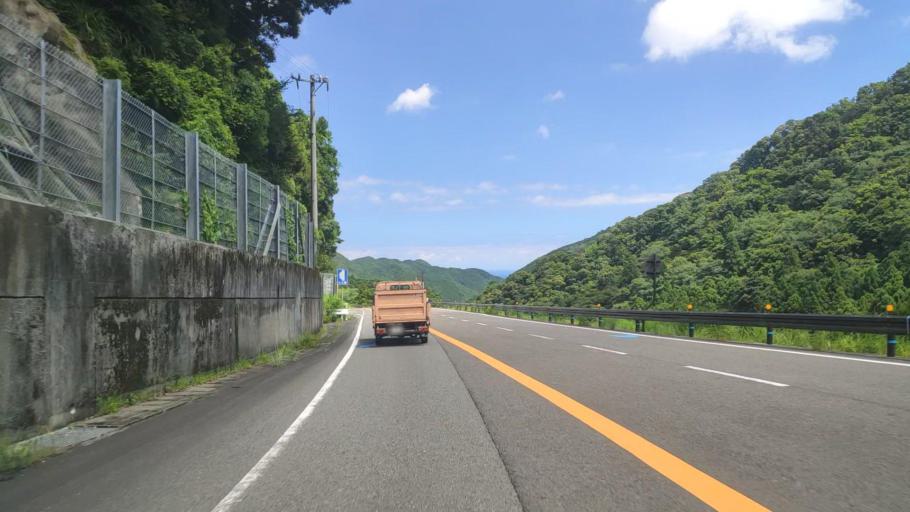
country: JP
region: Mie
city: Owase
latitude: 33.9216
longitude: 136.0969
